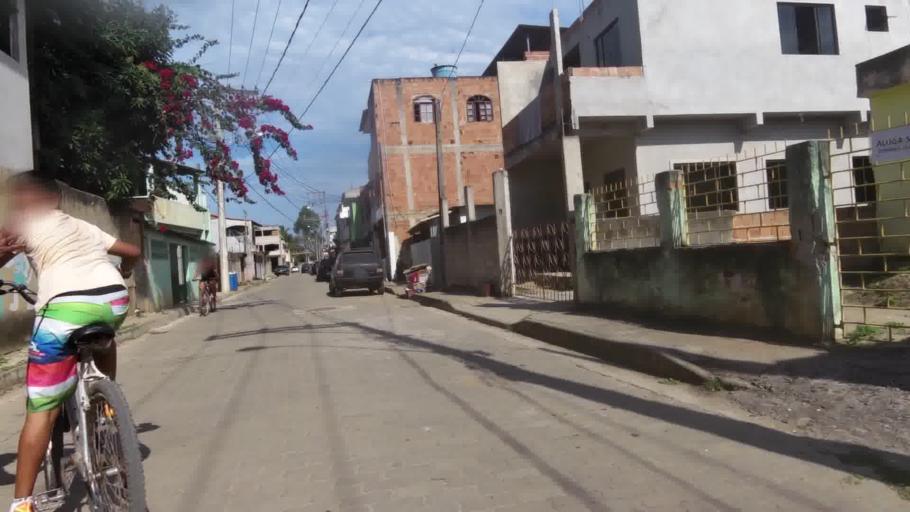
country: BR
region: Espirito Santo
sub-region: Piuma
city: Piuma
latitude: -20.8408
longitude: -40.7441
